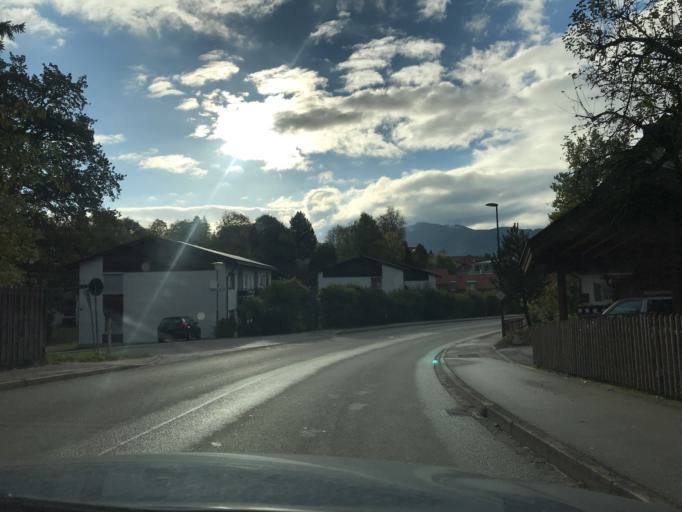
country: DE
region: Bavaria
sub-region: Upper Bavaria
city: Bad Toelz
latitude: 47.7672
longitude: 11.5625
